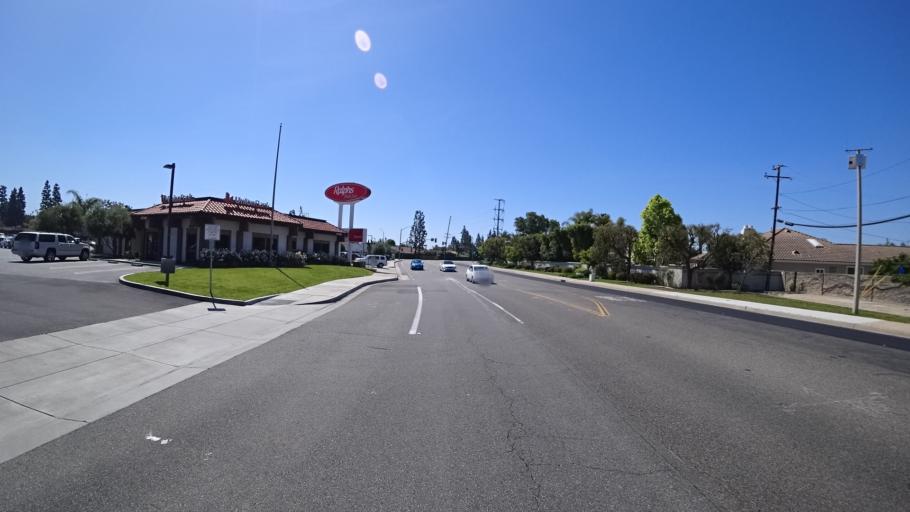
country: US
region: California
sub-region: Orange County
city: Villa Park
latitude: 33.8150
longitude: -117.8227
